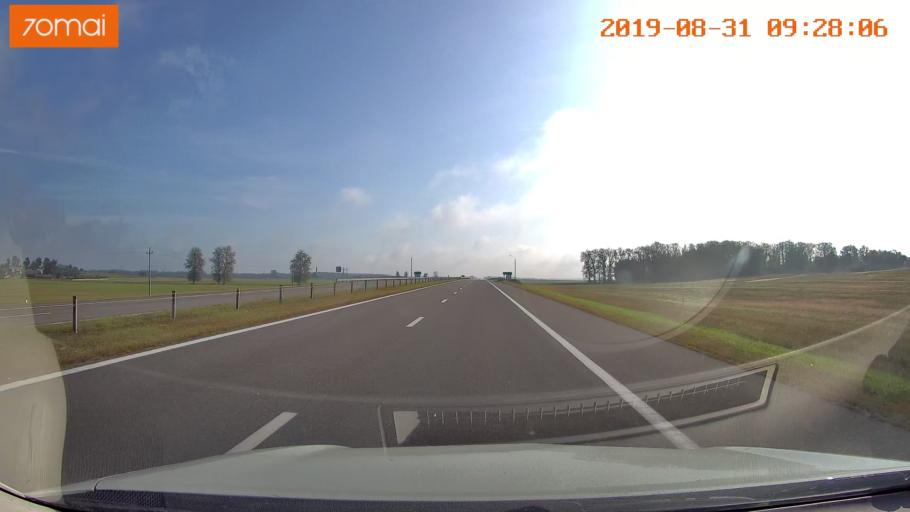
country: BY
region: Minsk
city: Byerazino
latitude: 53.8400
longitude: 29.0529
